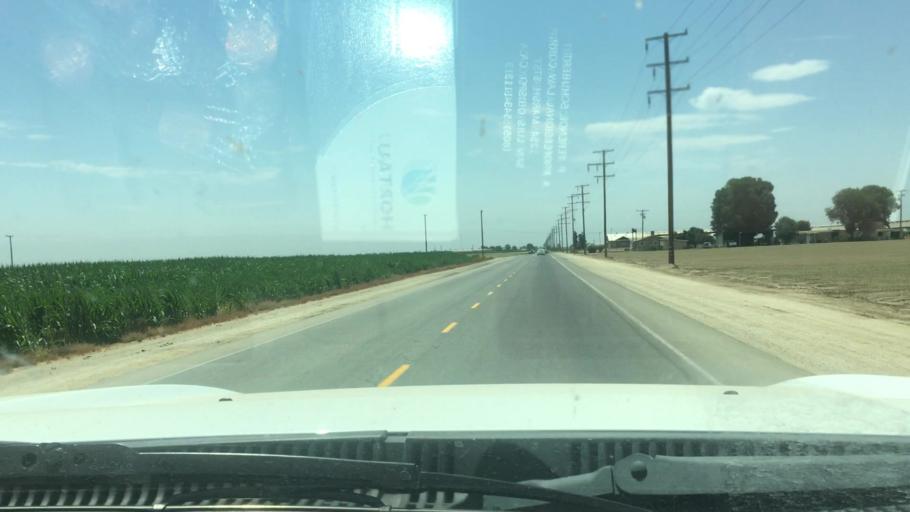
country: US
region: California
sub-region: Tulare County
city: Tipton
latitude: 36.0657
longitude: -119.2657
